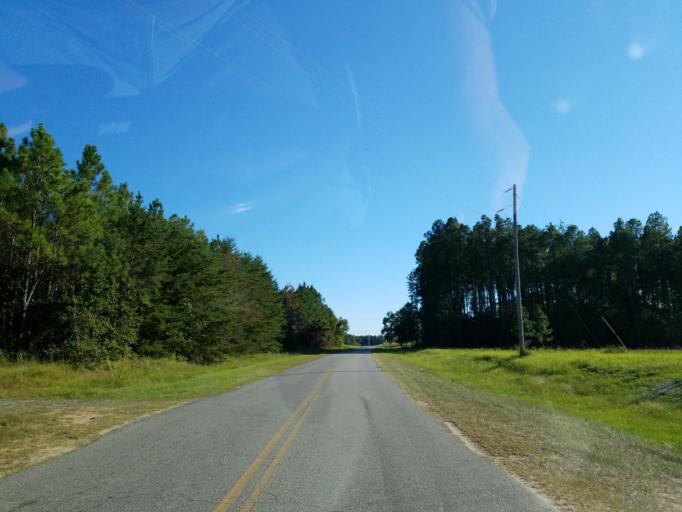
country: US
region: Georgia
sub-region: Dooly County
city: Vienna
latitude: 32.0742
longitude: -83.9558
